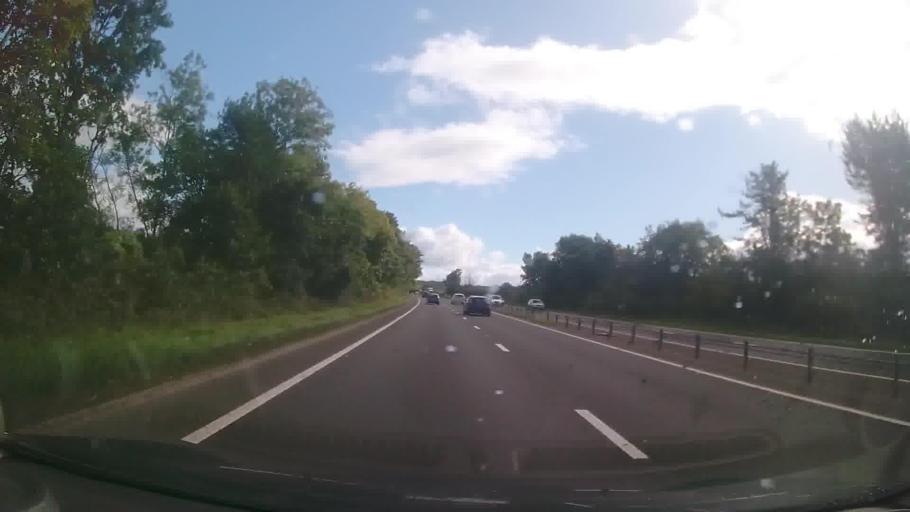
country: GB
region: Wales
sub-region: Carmarthenshire
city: Carmarthen
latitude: 51.8397
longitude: -4.2837
